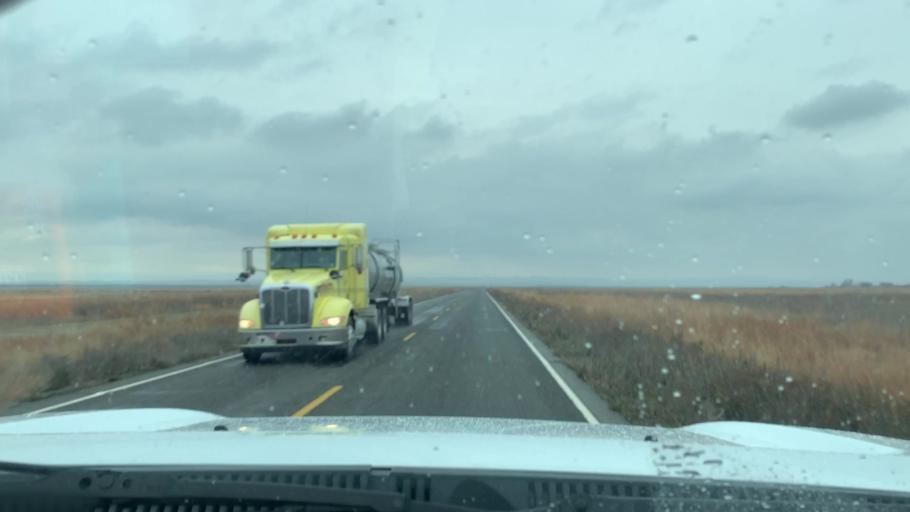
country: US
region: California
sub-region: Kings County
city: Kettleman City
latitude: 35.9340
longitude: -119.8037
